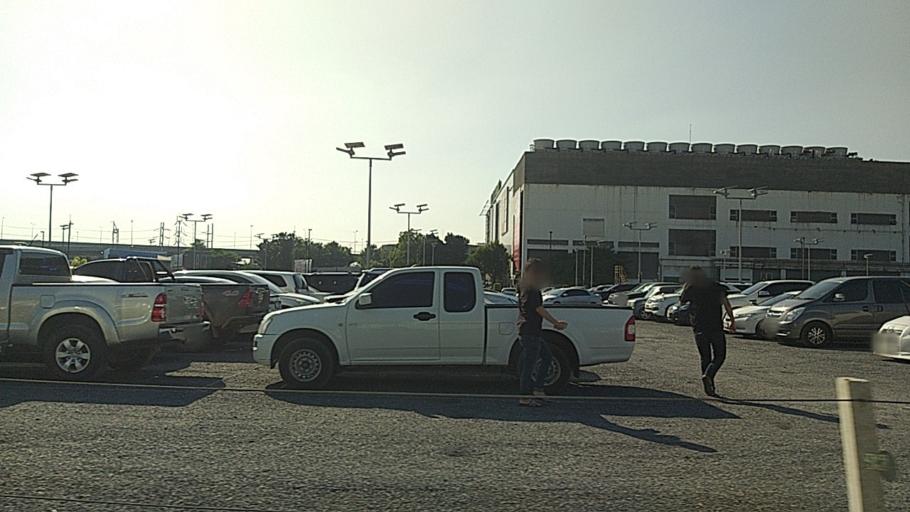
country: TH
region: Bangkok
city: Sai Mai
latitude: 13.9869
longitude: 100.6203
